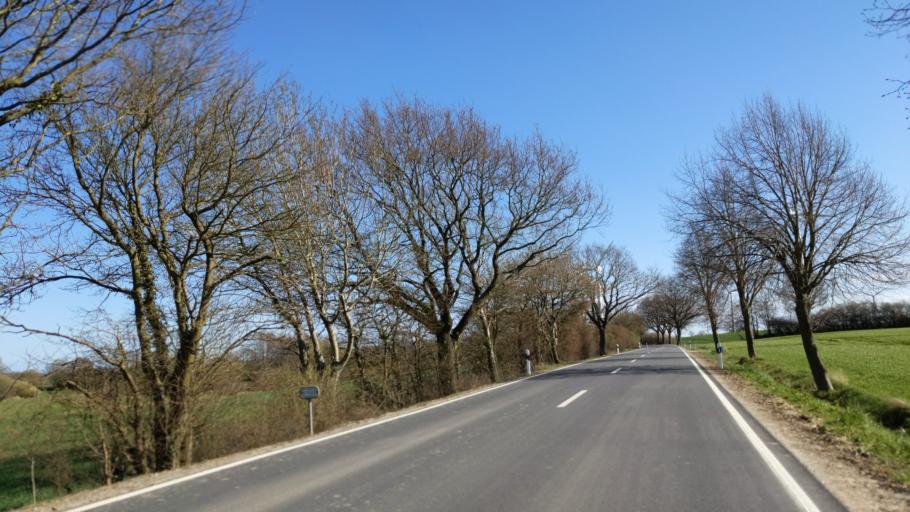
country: DE
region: Schleswig-Holstein
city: Eutin
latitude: 54.0702
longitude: 10.6369
